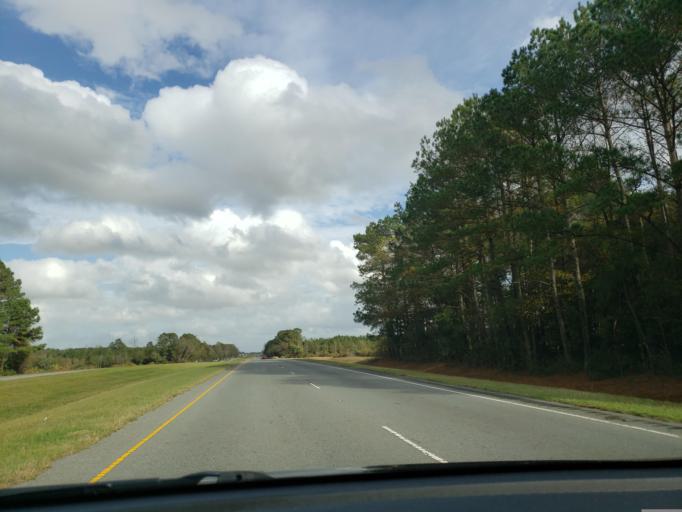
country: US
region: North Carolina
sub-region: Duplin County
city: Kenansville
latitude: 34.9314
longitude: -77.9956
